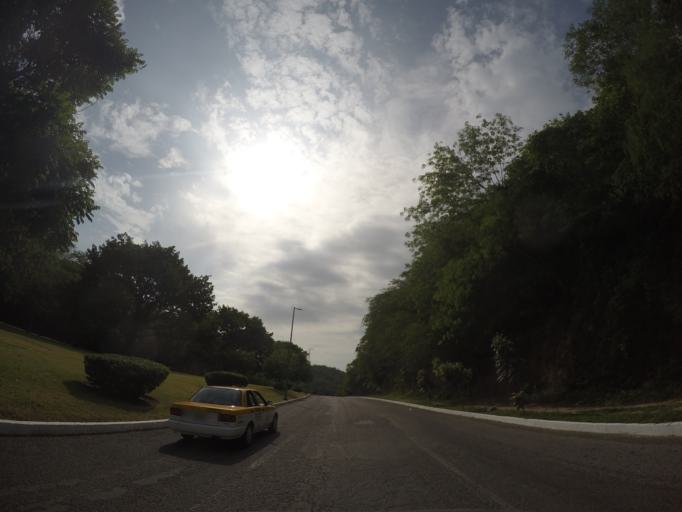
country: MX
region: Oaxaca
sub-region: Santa Maria Huatulco
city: Sector H Tres
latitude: 15.7713
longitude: -96.1430
